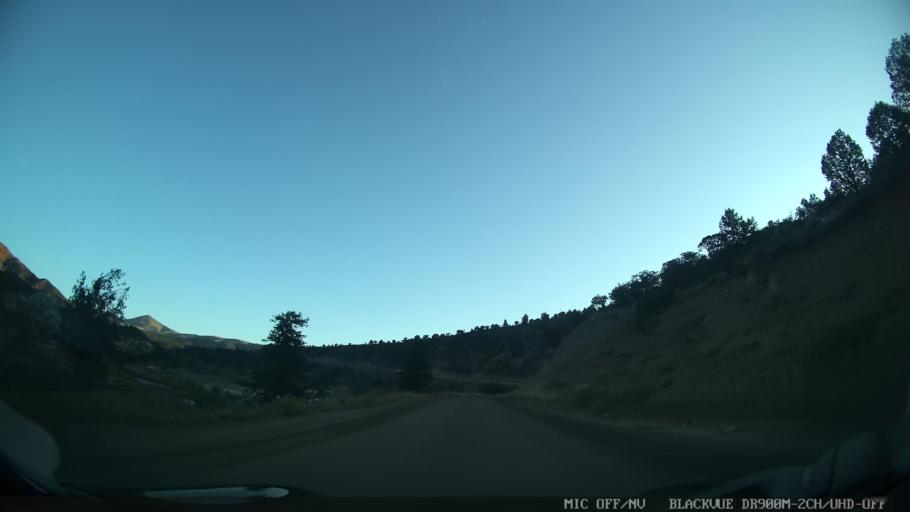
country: US
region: Colorado
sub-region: Eagle County
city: Edwards
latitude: 39.8925
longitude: -106.6094
